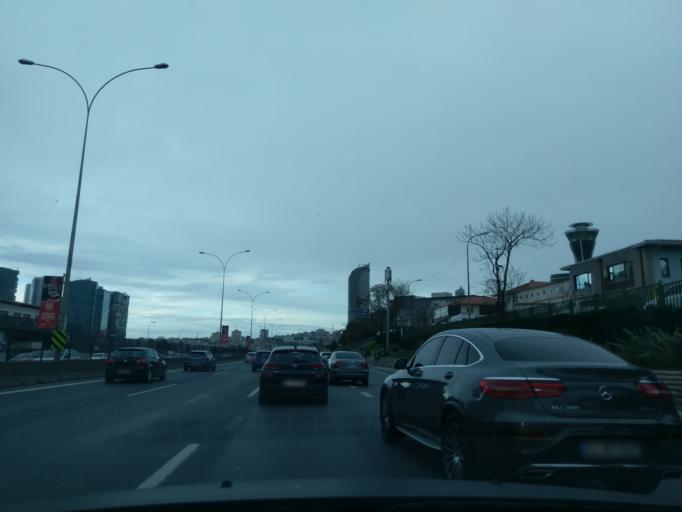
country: TR
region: Istanbul
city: UEskuedar
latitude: 40.9954
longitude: 29.0659
